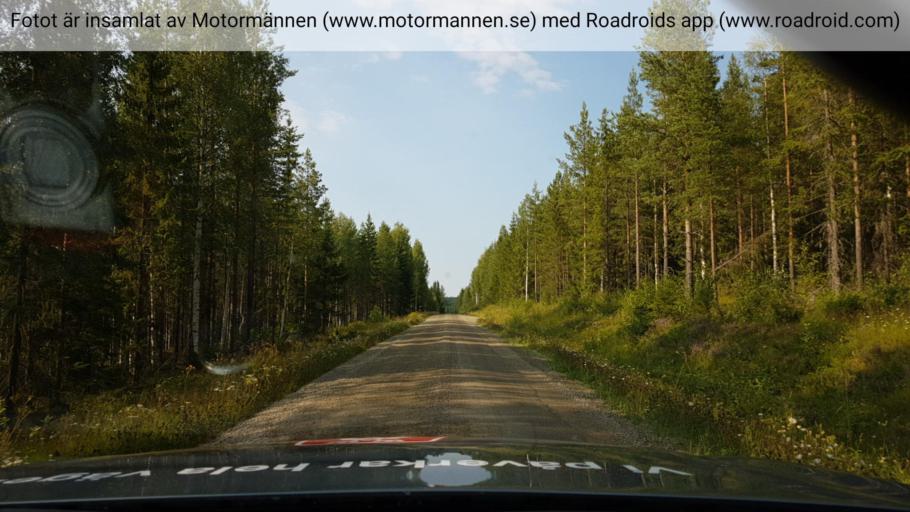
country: SE
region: Jaemtland
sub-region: Bergs Kommun
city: Hoverberg
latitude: 62.5144
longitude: 14.9155
